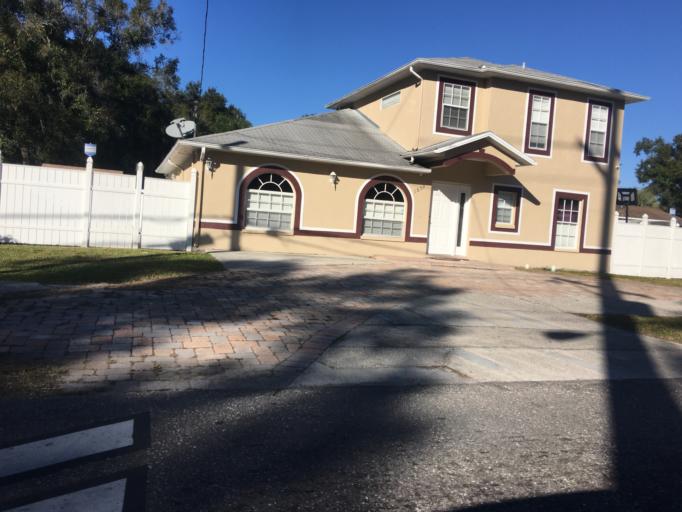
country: US
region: Florida
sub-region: Hillsborough County
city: Egypt Lake-Leto
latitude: 28.0181
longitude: -82.4779
